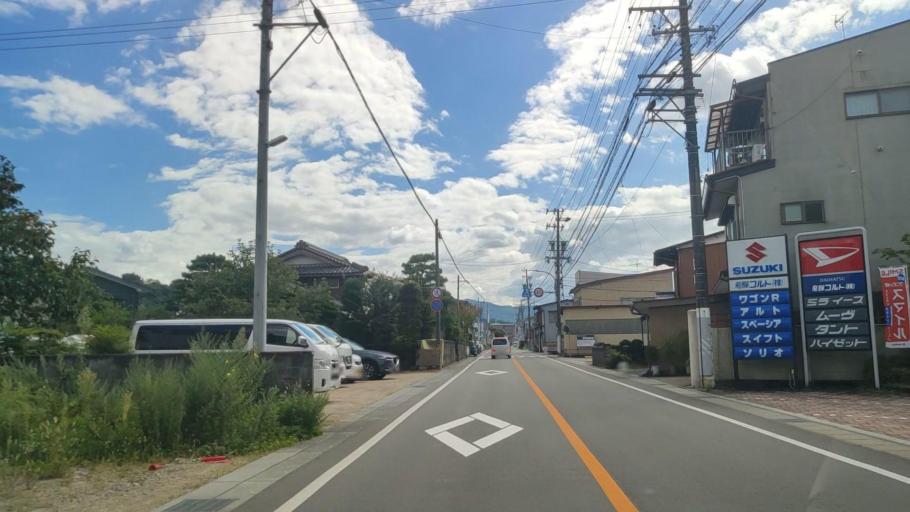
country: JP
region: Gifu
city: Takayama
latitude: 36.1572
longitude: 137.2533
